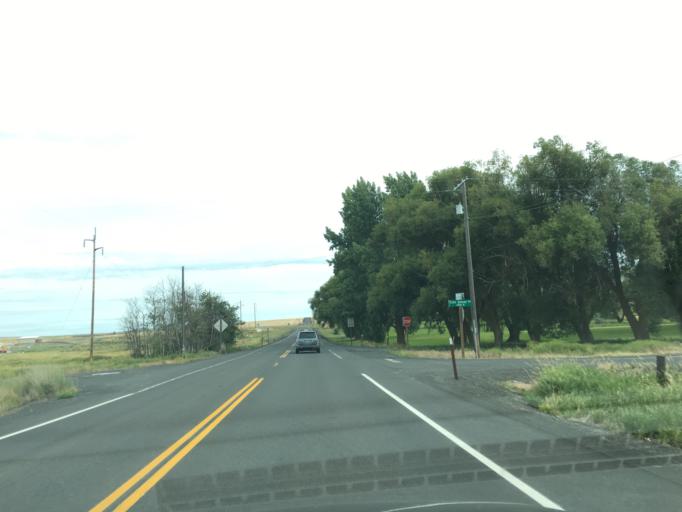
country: US
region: Washington
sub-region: Okanogan County
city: Coulee Dam
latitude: 47.7648
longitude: -118.7219
